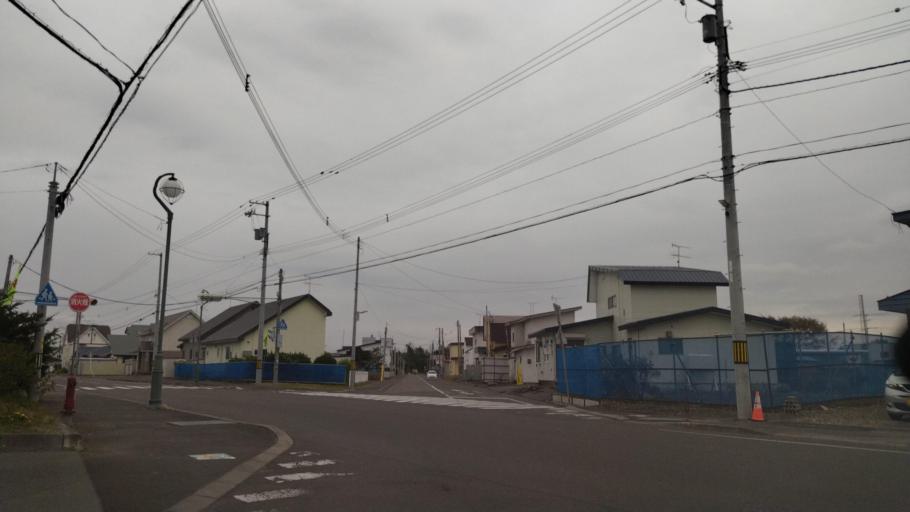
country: JP
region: Hokkaido
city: Otofuke
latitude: 43.2312
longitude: 143.2838
